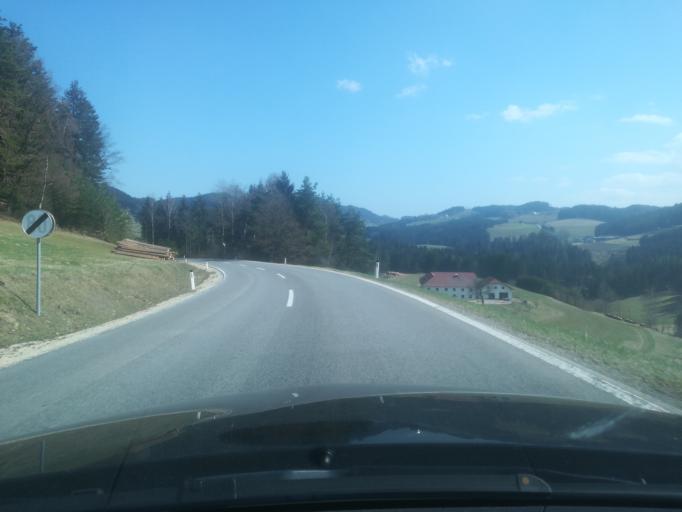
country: AT
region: Upper Austria
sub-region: Politischer Bezirk Perg
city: Sankt Georgen am Walde
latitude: 48.4171
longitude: 14.7614
